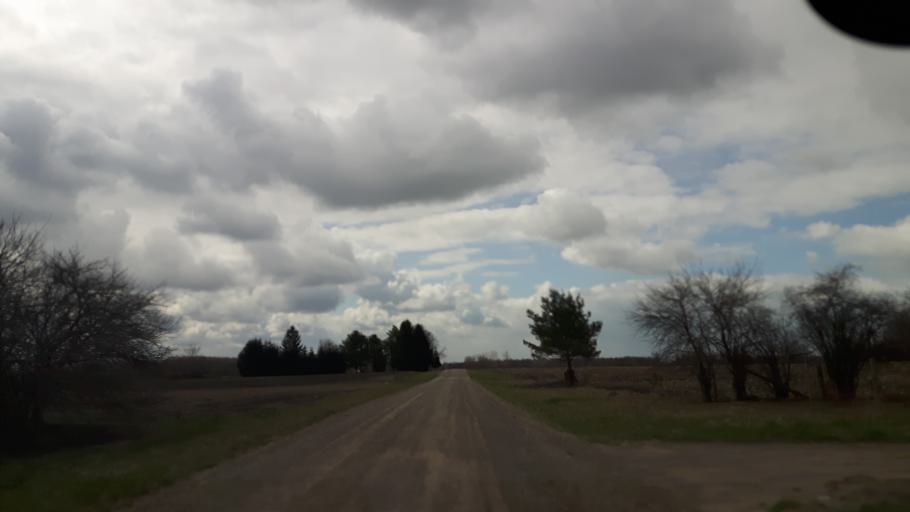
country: CA
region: Ontario
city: Bluewater
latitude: 43.5491
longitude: -81.6801
